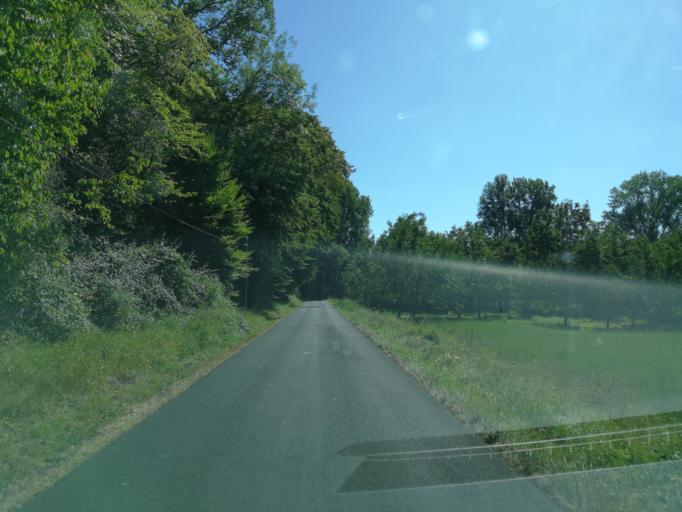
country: FR
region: Aquitaine
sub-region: Departement de la Dordogne
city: Eyvigues-et-Eybenes
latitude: 44.8719
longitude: 1.3821
